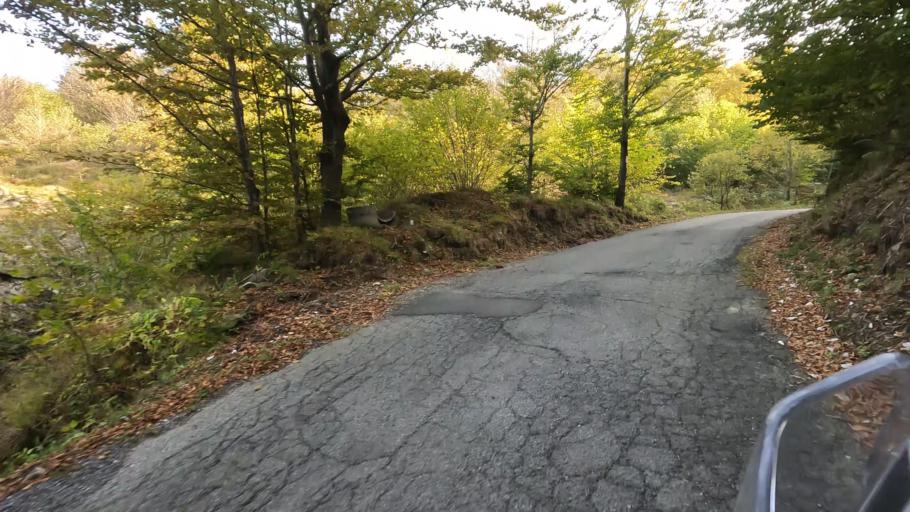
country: IT
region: Liguria
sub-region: Provincia di Genova
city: Sciarborasca
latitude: 44.4348
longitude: 8.5849
